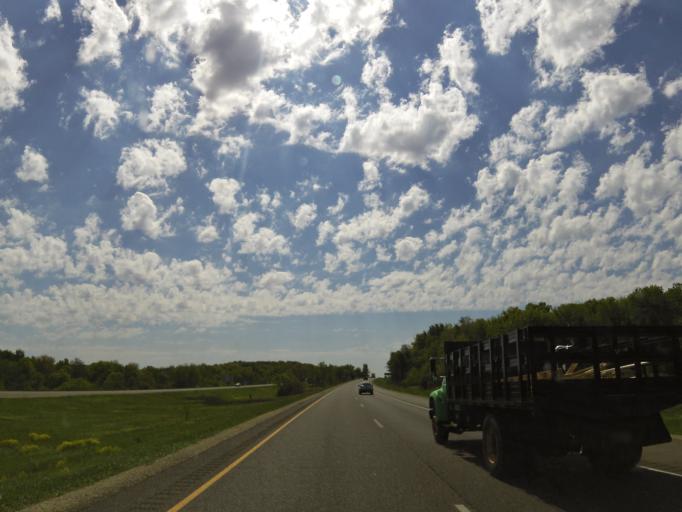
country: US
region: Wisconsin
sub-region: Eau Claire County
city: Eau Claire
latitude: 44.8336
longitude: -91.5832
